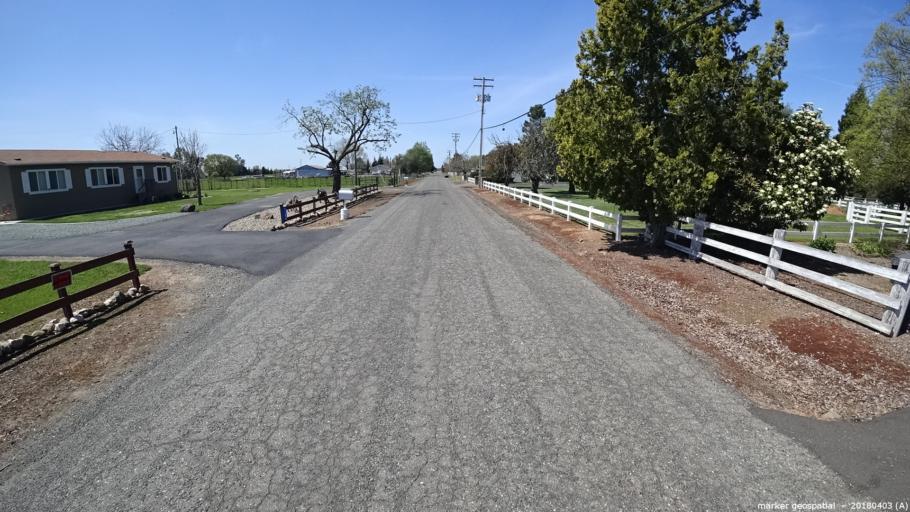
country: US
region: California
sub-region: Sacramento County
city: Wilton
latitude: 38.3873
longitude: -121.2651
